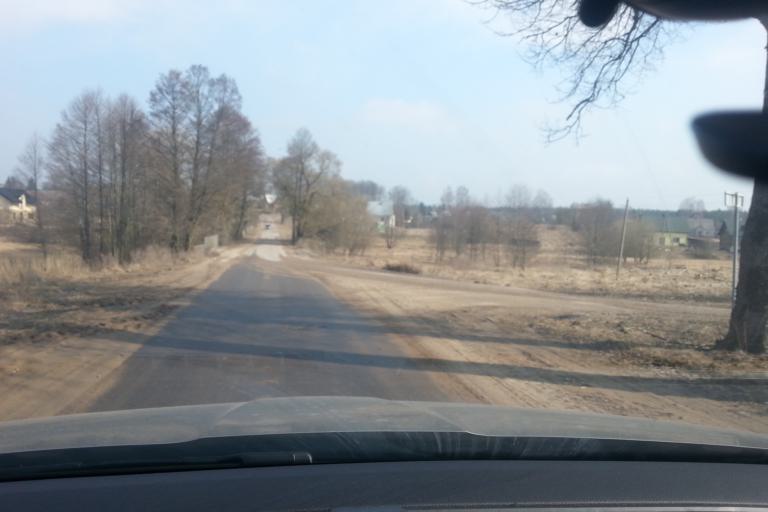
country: LT
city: Trakai
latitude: 54.4995
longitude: 24.9808
